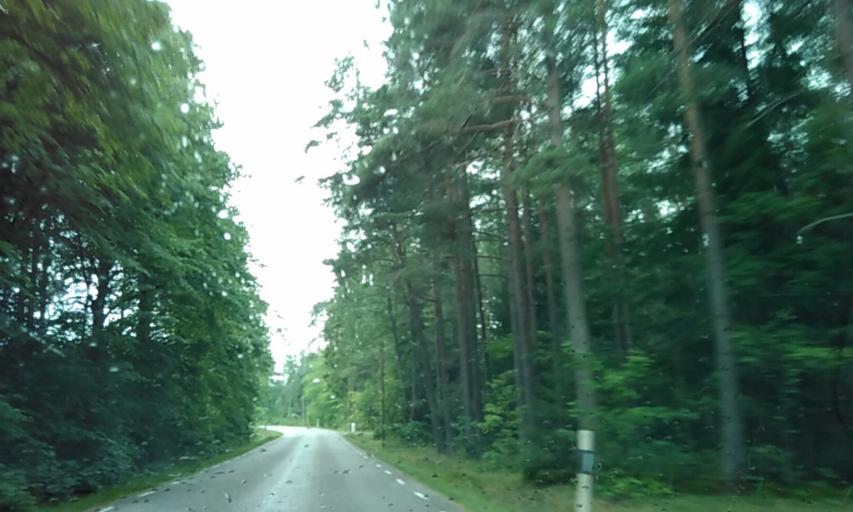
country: SE
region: Vaestra Goetaland
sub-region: Grastorps Kommun
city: Graestorp
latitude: 58.4610
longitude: 12.8006
